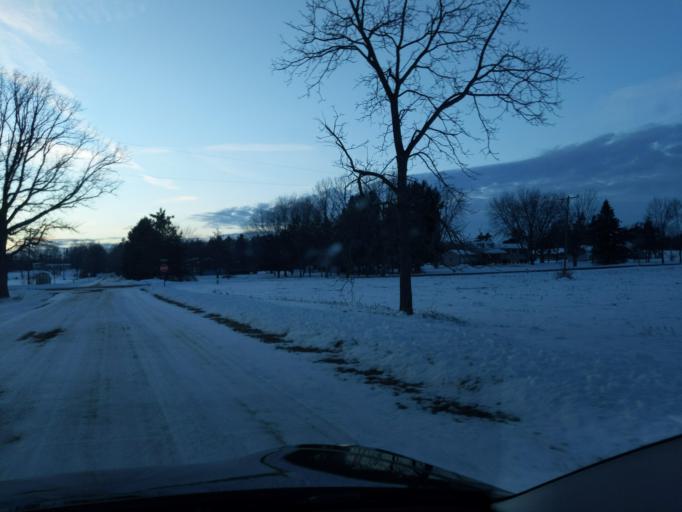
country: US
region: Michigan
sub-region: Ingham County
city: Mason
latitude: 42.5703
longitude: -84.3415
